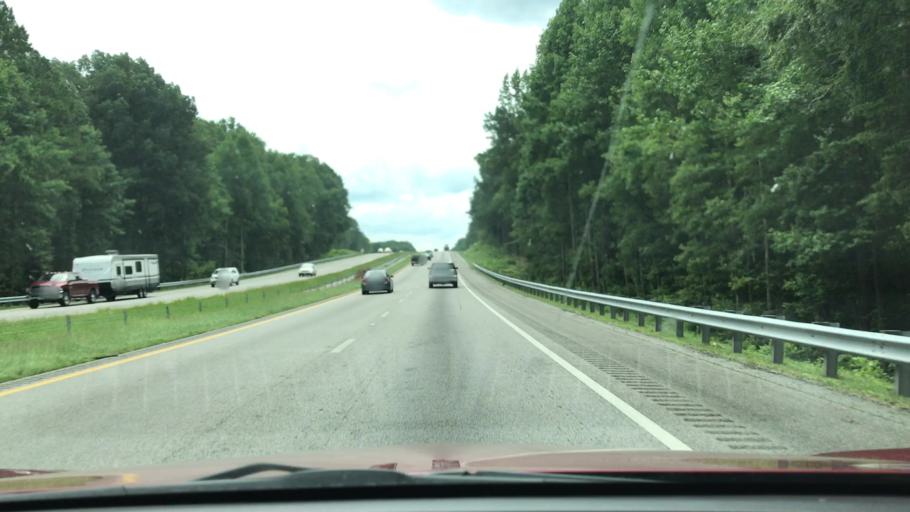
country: US
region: South Carolina
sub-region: Laurens County
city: Joanna
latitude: 34.4542
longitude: -81.7854
